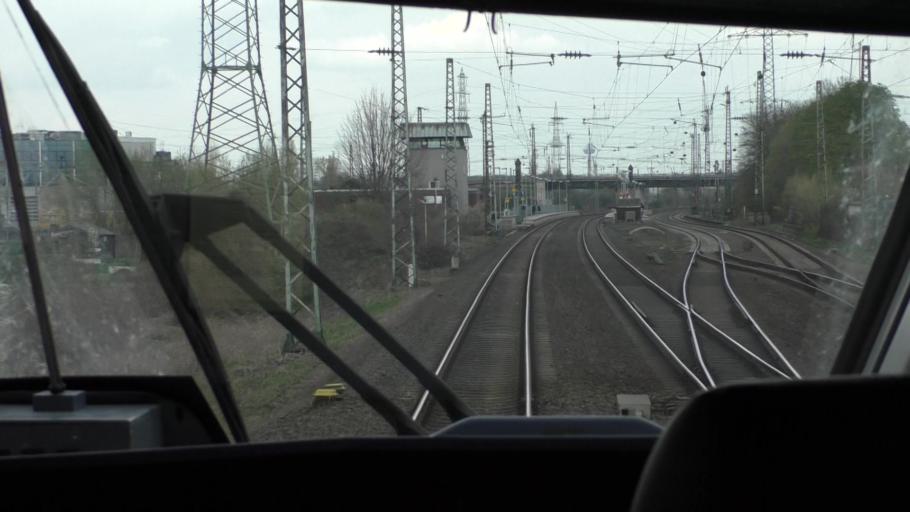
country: DE
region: North Rhine-Westphalia
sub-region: Regierungsbezirk Koln
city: Hurth
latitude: 50.8732
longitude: 6.9095
